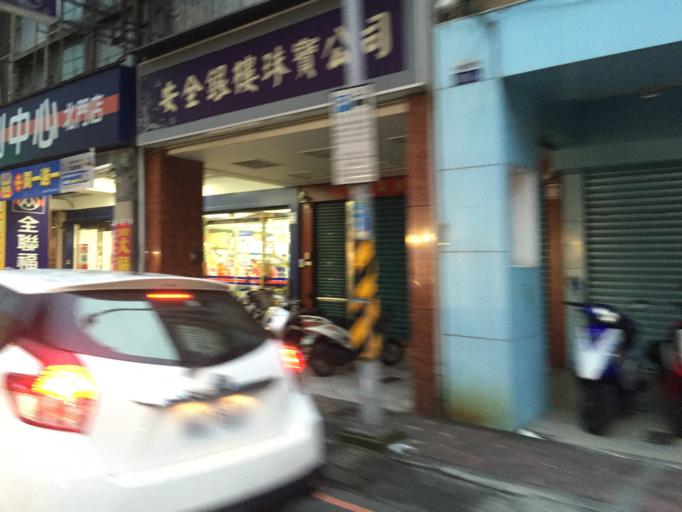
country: TW
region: Taiwan
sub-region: Yilan
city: Yilan
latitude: 24.7581
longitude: 121.7527
